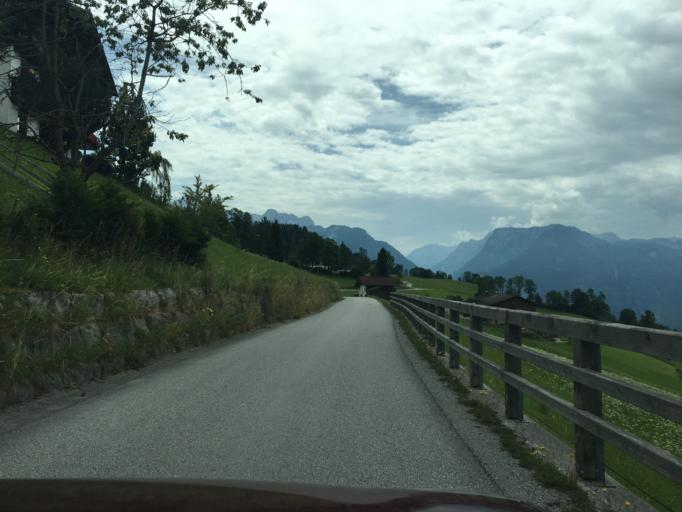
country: AT
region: Salzburg
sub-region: Politischer Bezirk Hallein
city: Golling an der Salzach
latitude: 47.6323
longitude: 13.1990
